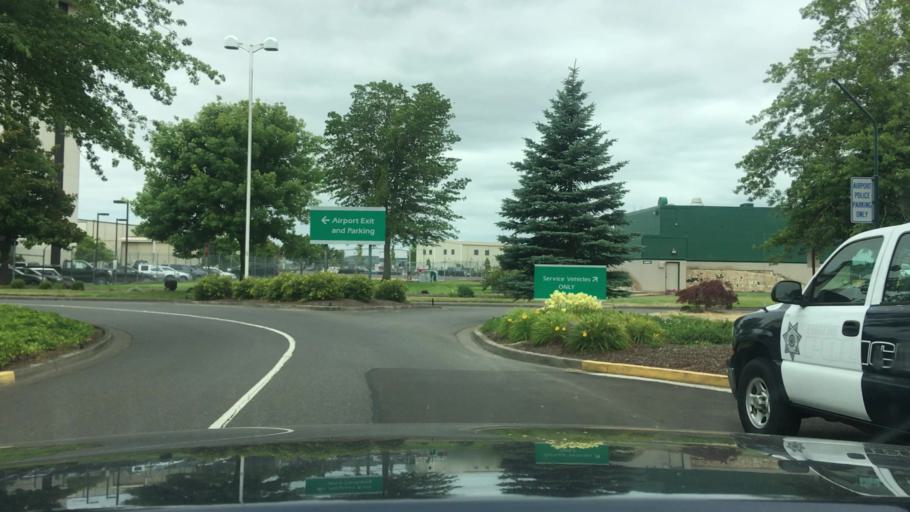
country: US
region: Oregon
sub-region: Lane County
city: Junction City
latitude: 44.1184
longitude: -123.2126
